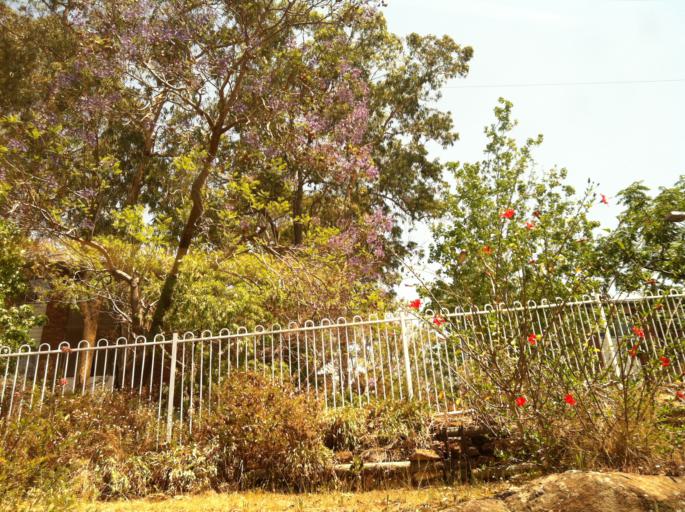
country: AU
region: New South Wales
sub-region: Blue Mountains Municipality
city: Glenbrook
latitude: -33.7741
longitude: 150.6428
